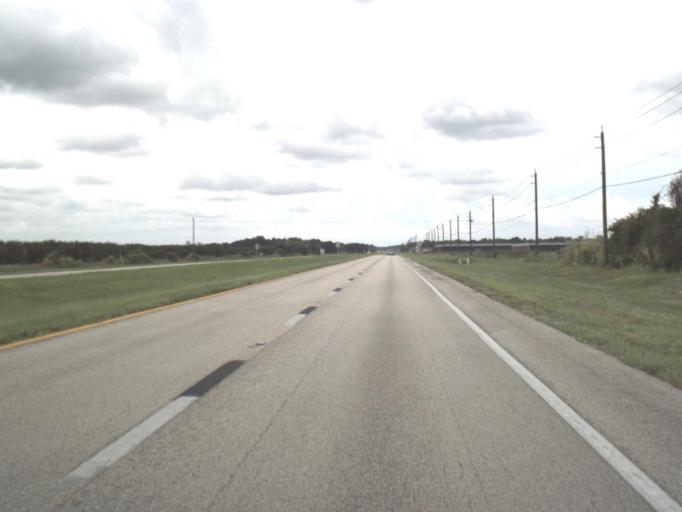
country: US
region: Florida
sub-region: Lee County
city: Alva
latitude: 26.7093
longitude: -81.5847
